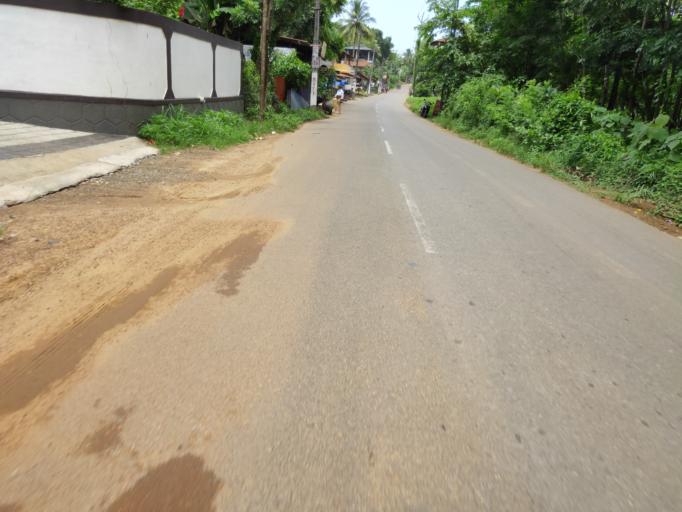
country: IN
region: Kerala
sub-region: Malappuram
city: Manjeri
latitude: 11.2162
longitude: 76.2610
